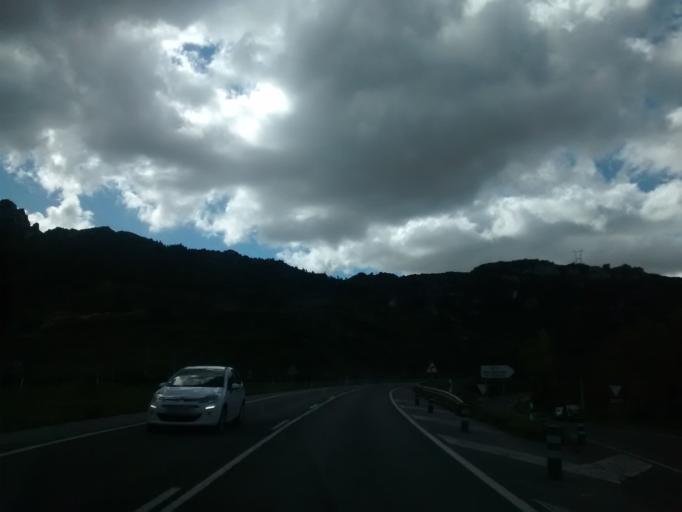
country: ES
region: La Rioja
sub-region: Provincia de La Rioja
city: Brinas
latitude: 42.6303
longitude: -2.8422
